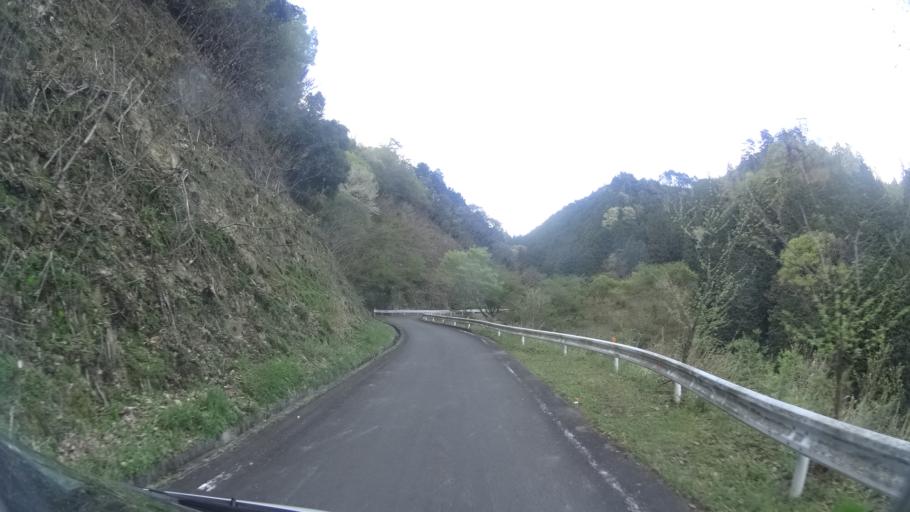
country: JP
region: Kyoto
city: Ayabe
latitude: 35.2580
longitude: 135.3195
